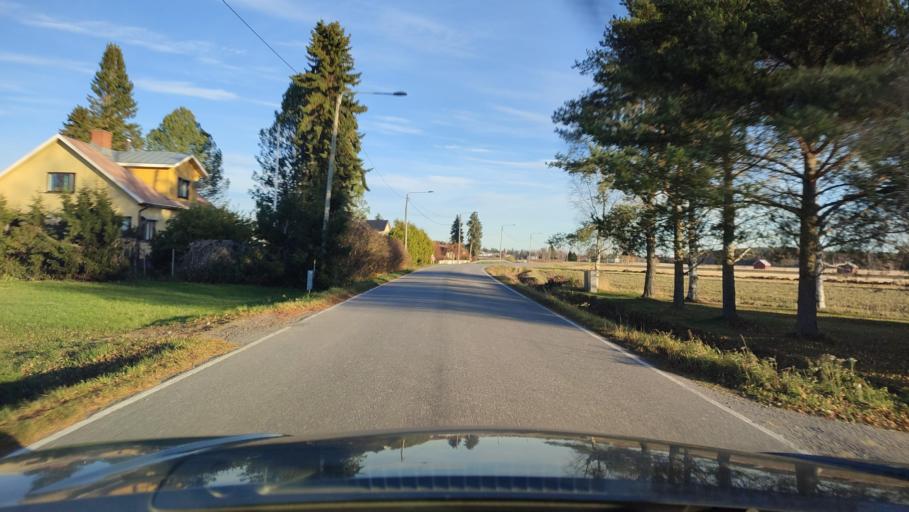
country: FI
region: Ostrobothnia
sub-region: Vaasa
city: Ristinummi
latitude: 63.0006
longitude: 21.6930
